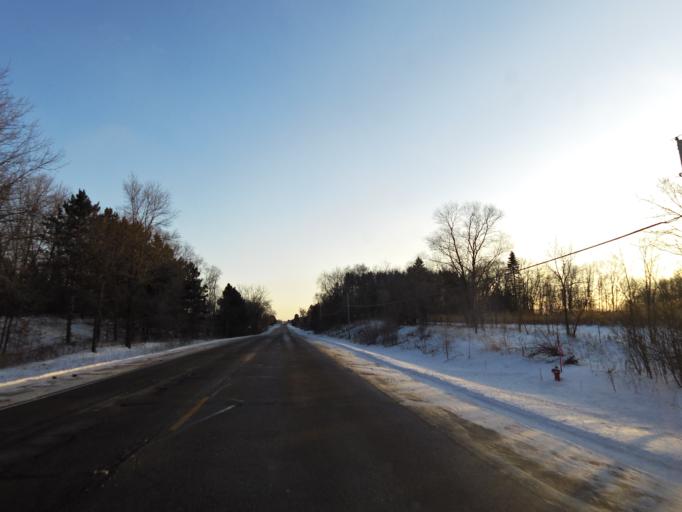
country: US
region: Minnesota
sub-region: Washington County
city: Lake Elmo
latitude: 44.9720
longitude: -92.8831
